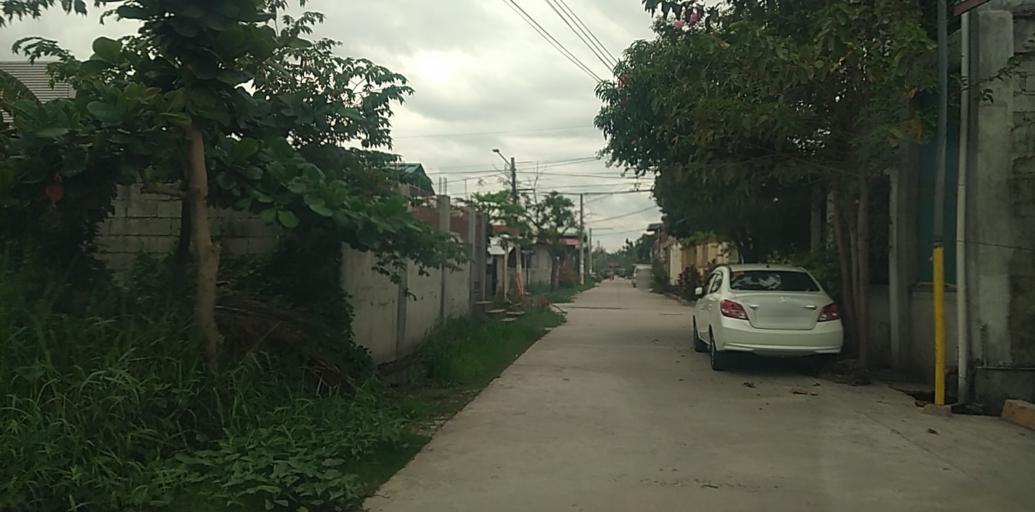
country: PH
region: Central Luzon
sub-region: Province of Pampanga
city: San Fernando
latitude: 15.0002
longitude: 120.7032
